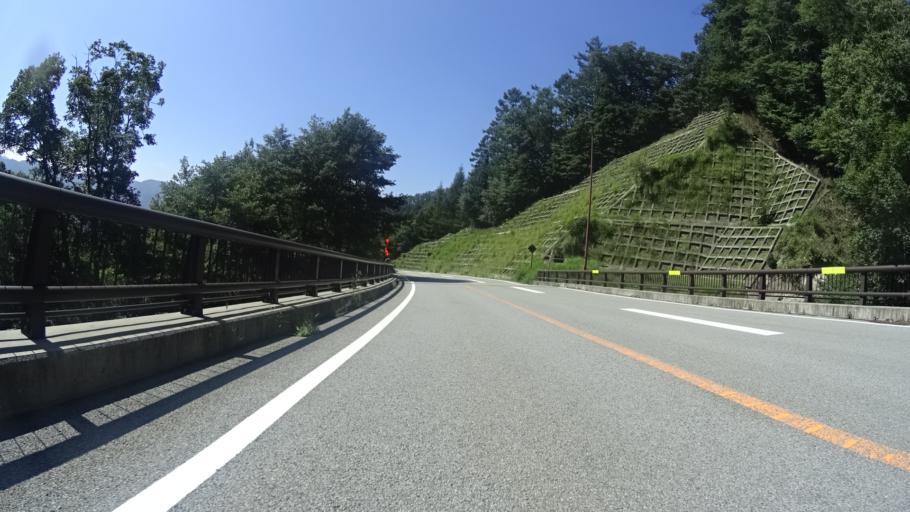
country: JP
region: Yamanashi
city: Enzan
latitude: 35.7605
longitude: 138.8060
